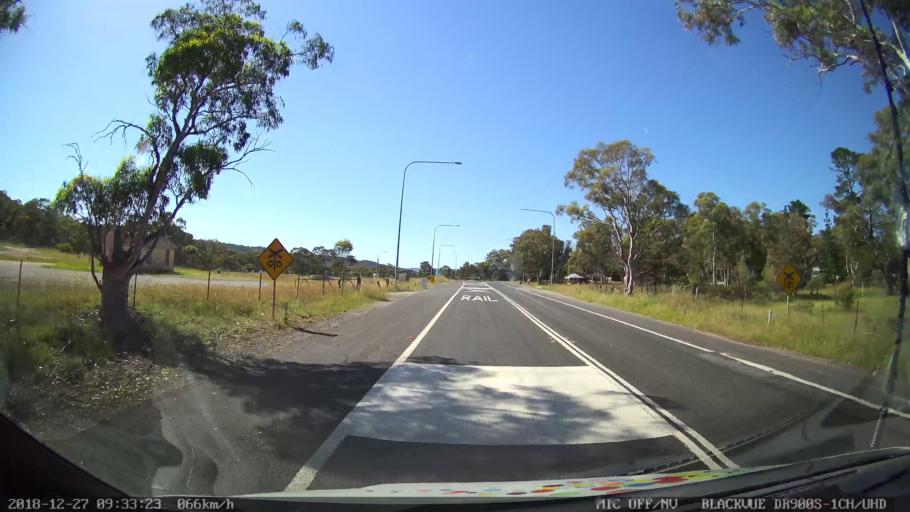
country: AU
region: New South Wales
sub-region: Lithgow
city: Portland
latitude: -33.2181
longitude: 150.0213
